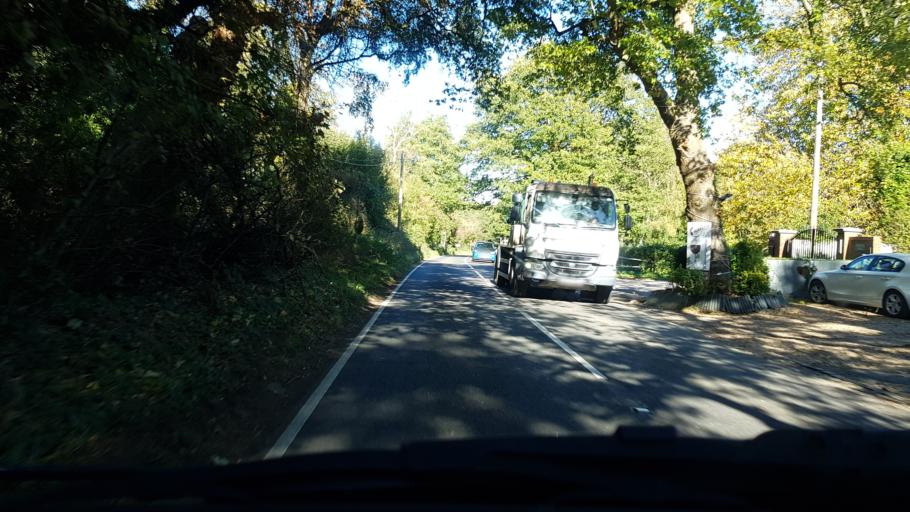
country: GB
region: England
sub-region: Surrey
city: Chilworth
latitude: 51.2365
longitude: -0.5063
